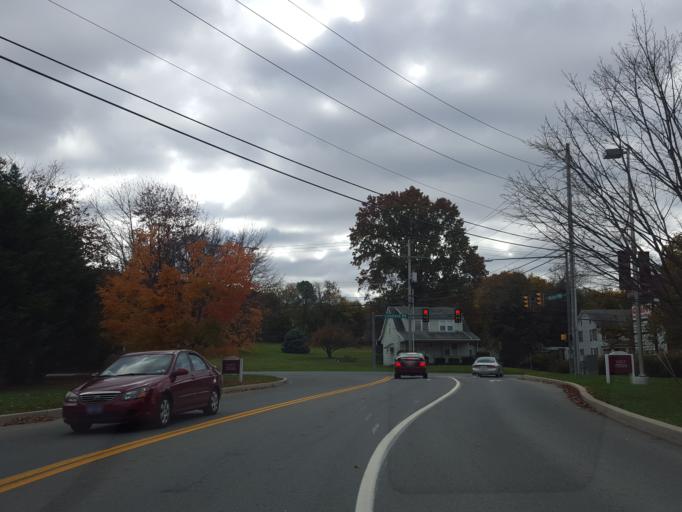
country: US
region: Pennsylvania
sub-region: York County
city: Yoe
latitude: 39.9178
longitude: -76.6259
